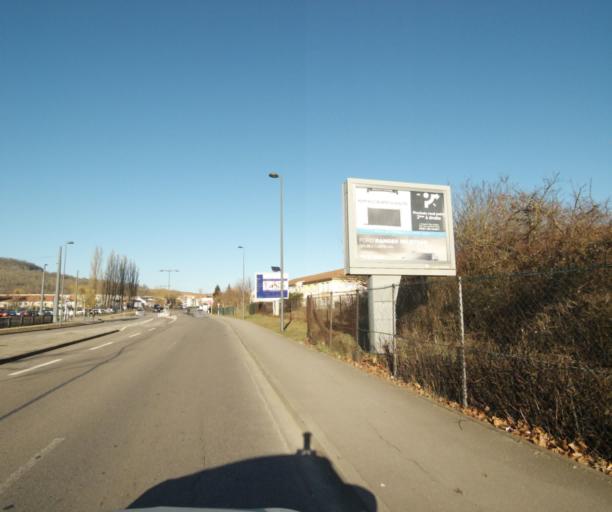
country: FR
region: Lorraine
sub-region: Departement de Meurthe-et-Moselle
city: Essey-les-Nancy
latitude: 48.7009
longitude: 6.2250
